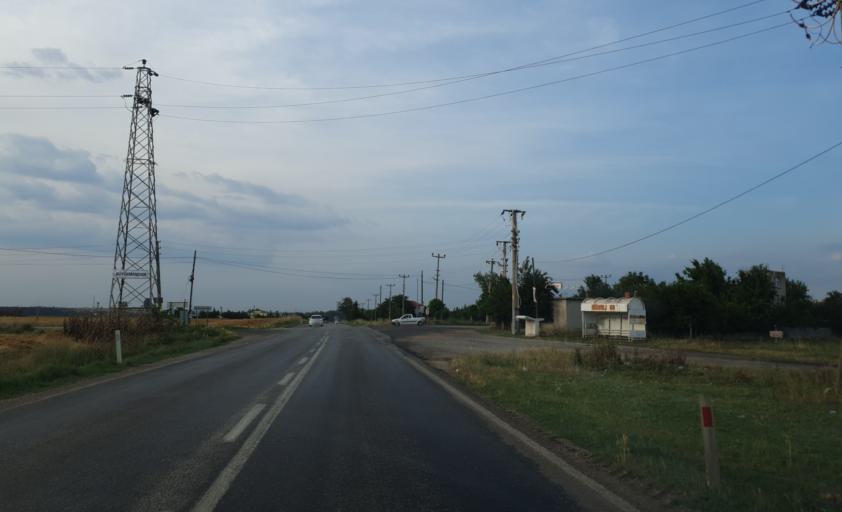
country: TR
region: Kirklareli
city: Babaeski
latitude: 41.3466
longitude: 27.1418
